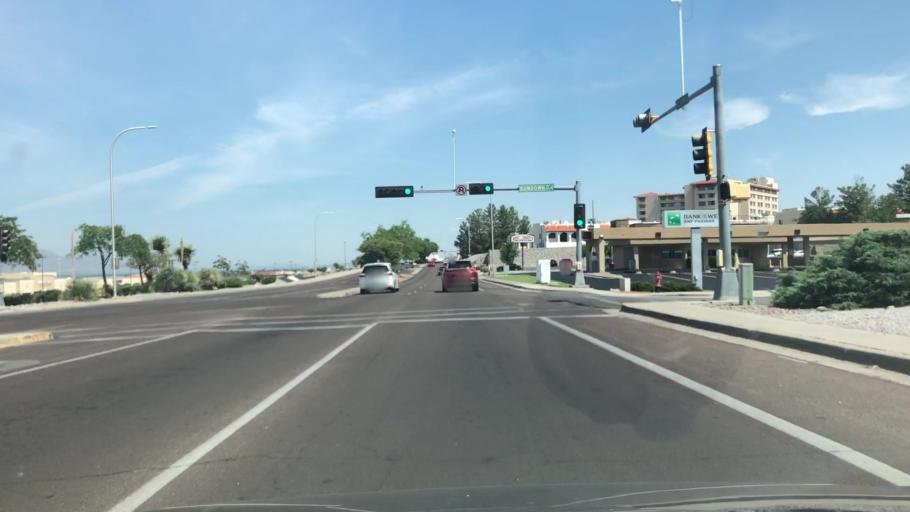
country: US
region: New Mexico
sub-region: Dona Ana County
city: University Park
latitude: 32.3096
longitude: -106.7402
